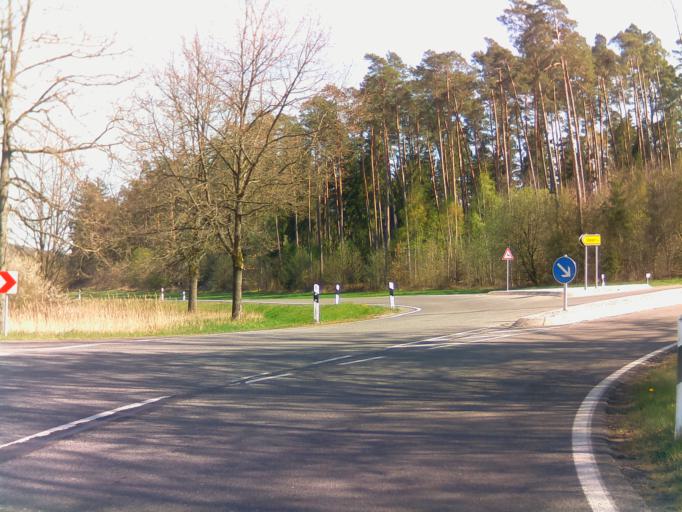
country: DE
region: Bavaria
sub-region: Regierungsbezirk Unterfranken
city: Burgpreppach
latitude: 50.1364
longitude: 10.5960
